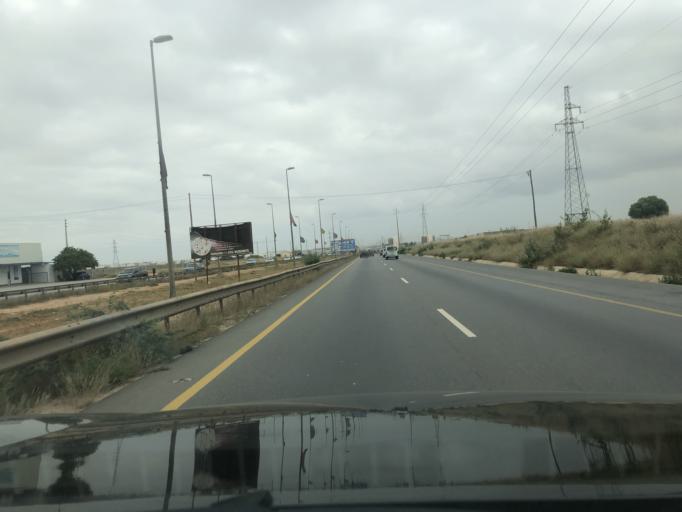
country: AO
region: Luanda
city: Luanda
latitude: -8.9737
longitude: 13.2289
